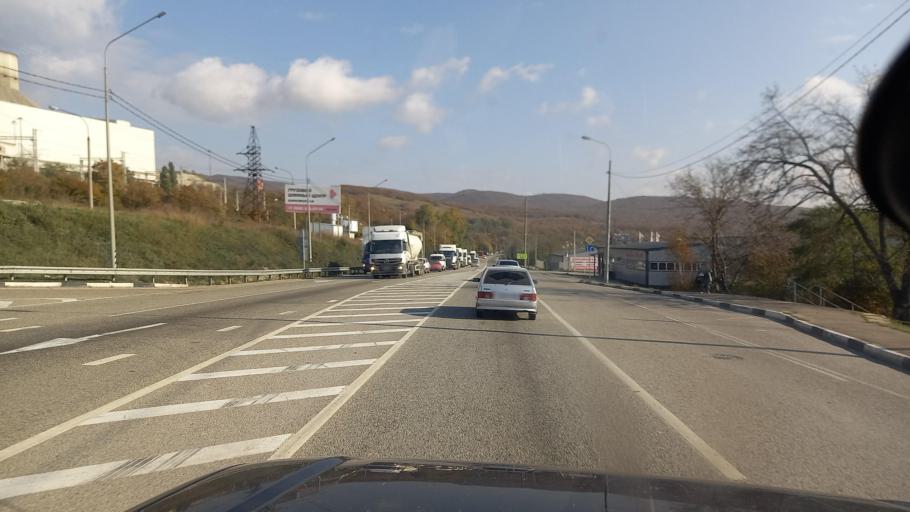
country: RU
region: Krasnodarskiy
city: Verkhnebakanskiy
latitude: 44.8418
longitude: 37.6703
